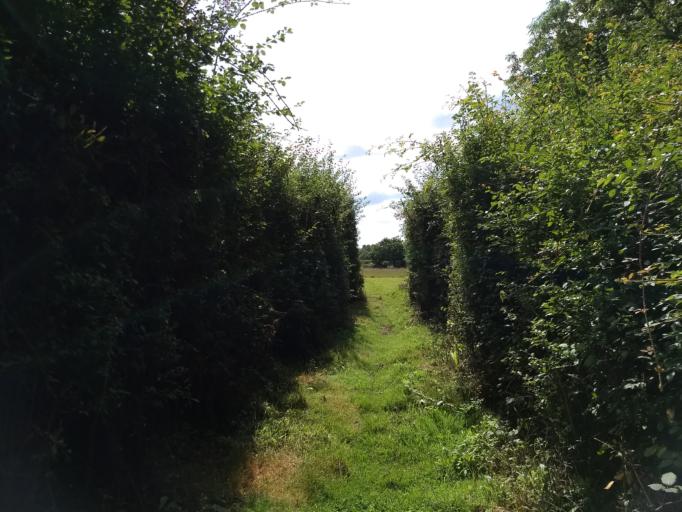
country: GB
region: England
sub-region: Isle of Wight
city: Ryde
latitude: 50.7075
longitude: -1.1494
